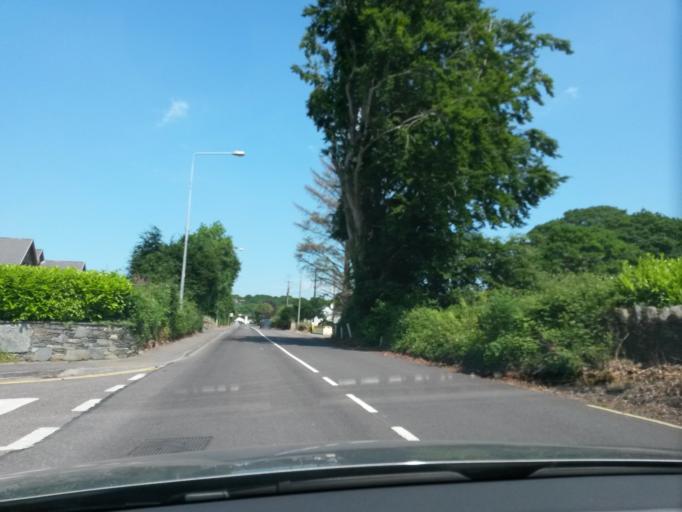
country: IE
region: Munster
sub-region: Ciarrai
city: Cill Airne
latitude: 52.0550
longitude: -9.4830
